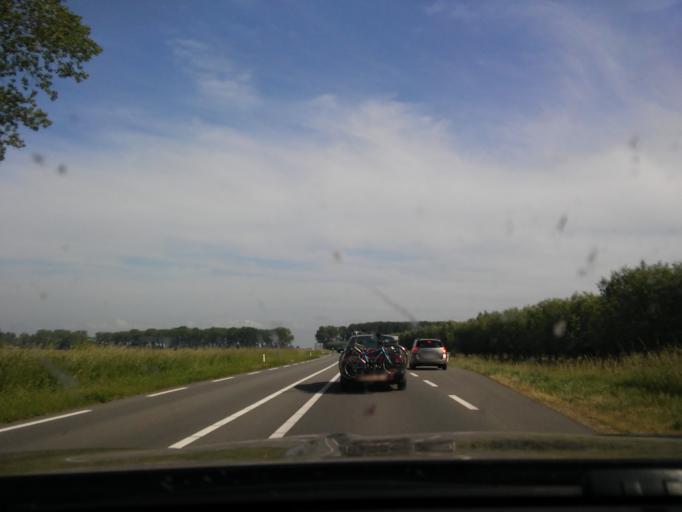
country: NL
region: Zeeland
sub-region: Gemeente Sluis
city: Sluis
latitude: 51.3108
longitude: 3.3655
